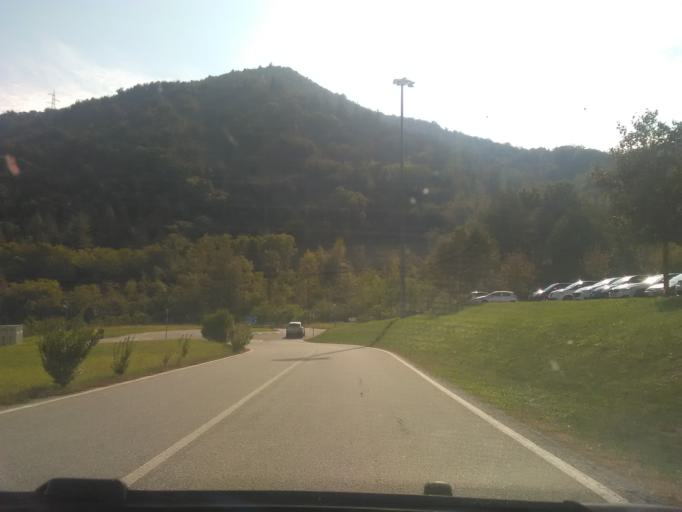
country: IT
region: Piedmont
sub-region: Provincia di Vercelli
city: Borgosesia
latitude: 45.7124
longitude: 8.2625
